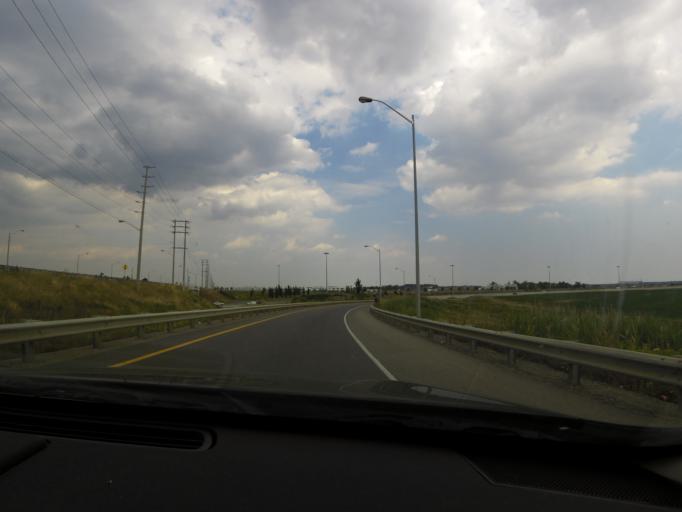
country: CA
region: Ontario
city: Brampton
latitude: 43.7553
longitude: -79.8000
